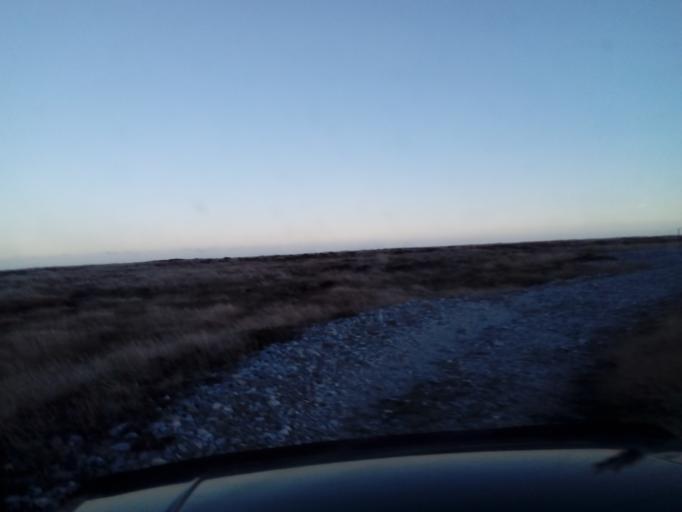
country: FK
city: Stanley
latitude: -51.7028
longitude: -57.8405
